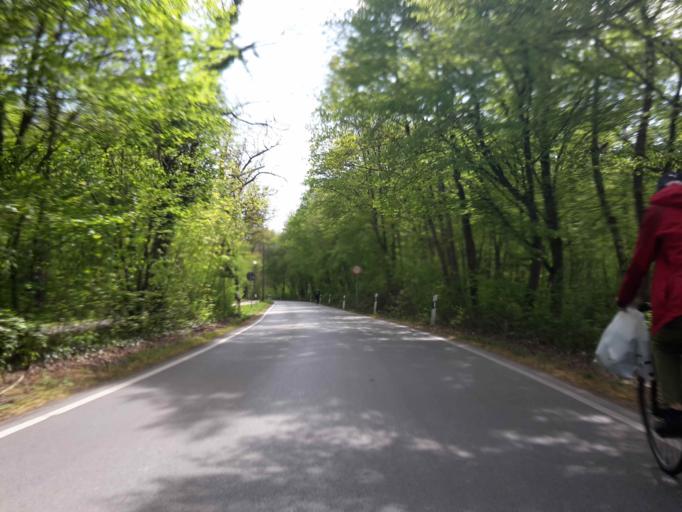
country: DE
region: Bavaria
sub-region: Upper Bavaria
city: Pasing
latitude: 48.1692
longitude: 11.4939
